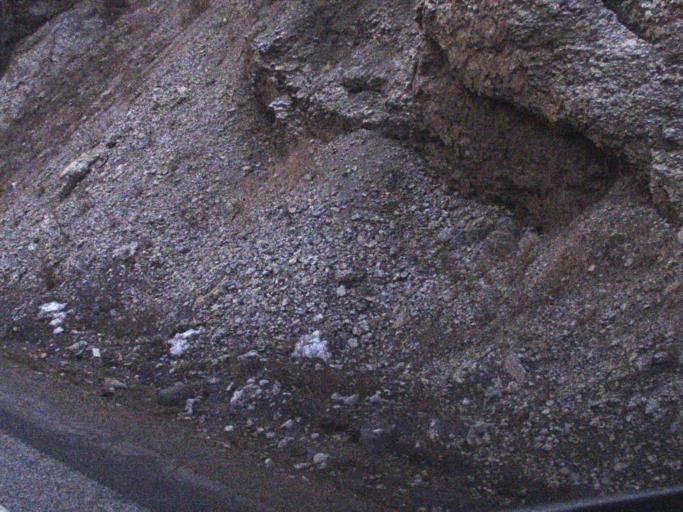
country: US
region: Washington
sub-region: Ferry County
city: Republic
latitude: 48.6102
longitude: -118.4479
